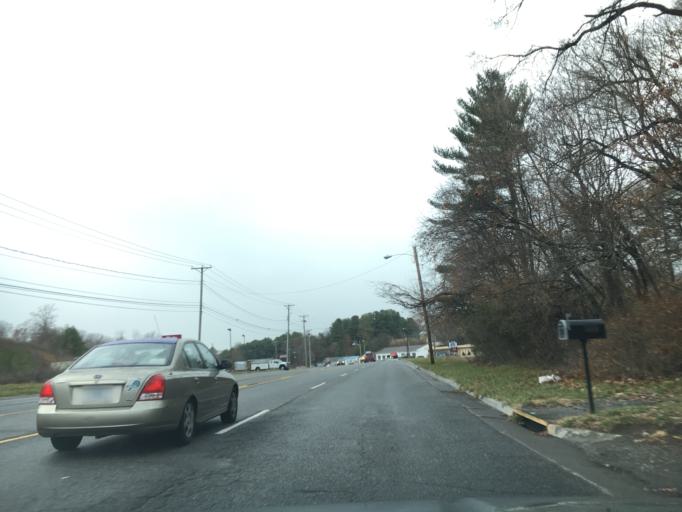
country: US
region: Virginia
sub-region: Montgomery County
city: Christiansburg
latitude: 37.1332
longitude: -80.3834
